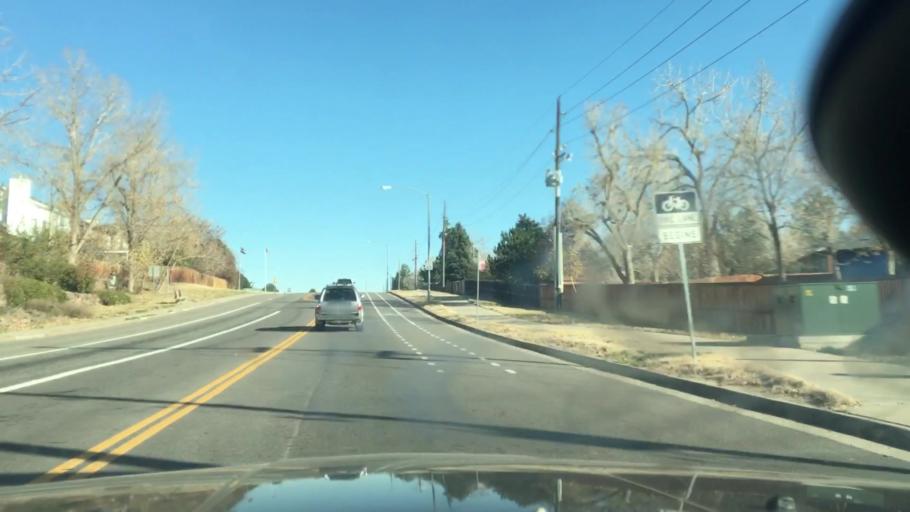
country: US
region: Colorado
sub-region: Arapahoe County
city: Glendale
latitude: 39.6676
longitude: -104.9032
